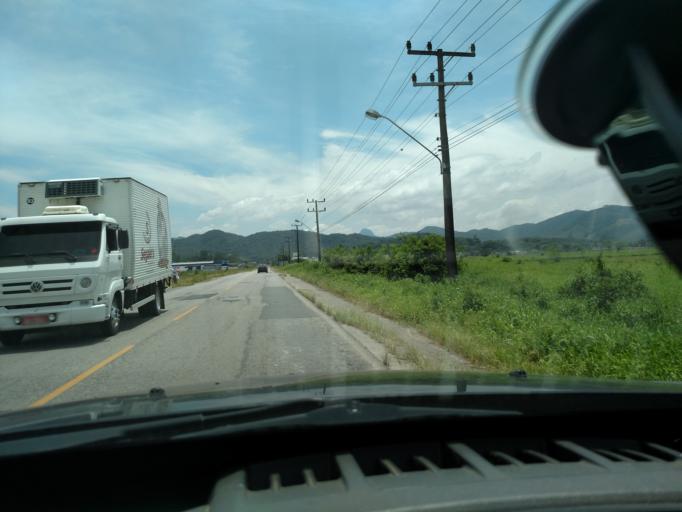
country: BR
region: Santa Catarina
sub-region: Gaspar
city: Gaspar
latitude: -26.9216
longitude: -48.9329
